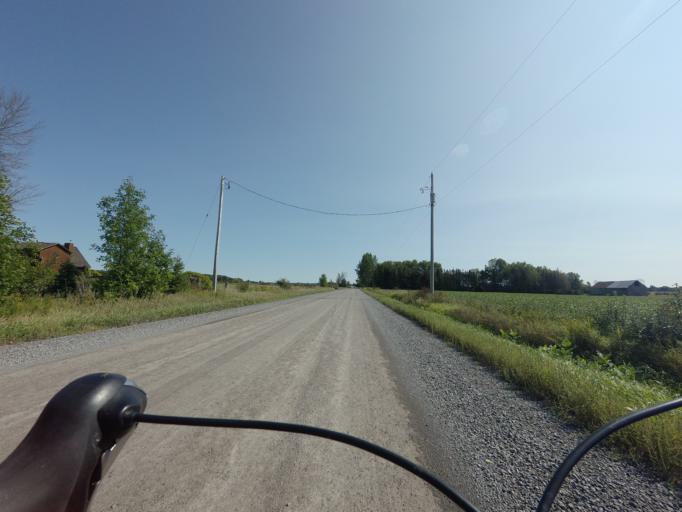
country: CA
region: Ontario
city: Arnprior
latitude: 45.3855
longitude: -76.1573
